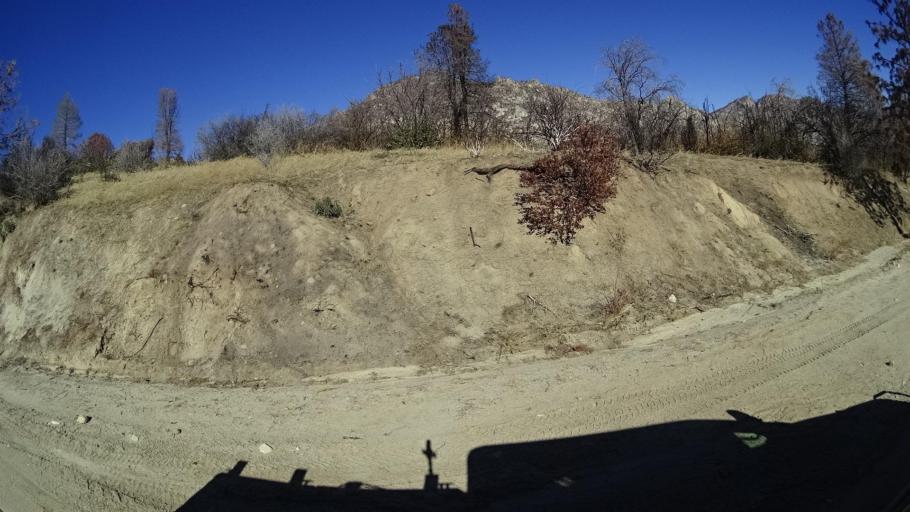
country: US
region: California
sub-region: Kern County
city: Alta Sierra
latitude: 35.7154
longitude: -118.5234
